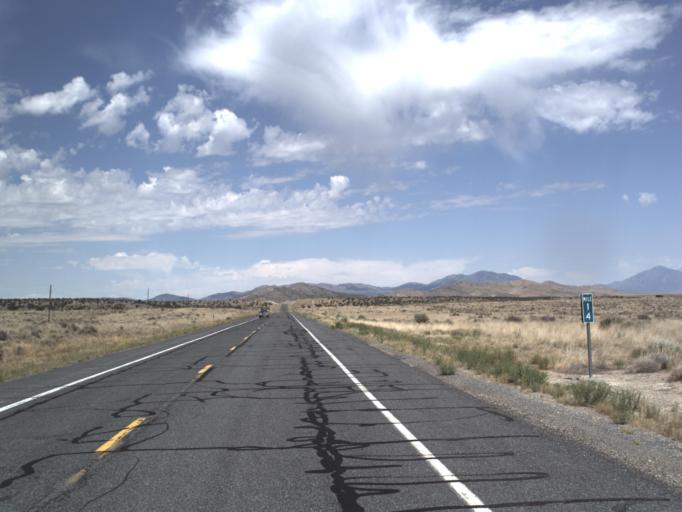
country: US
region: Utah
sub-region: Utah County
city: Eagle Mountain
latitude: 40.0562
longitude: -112.3039
